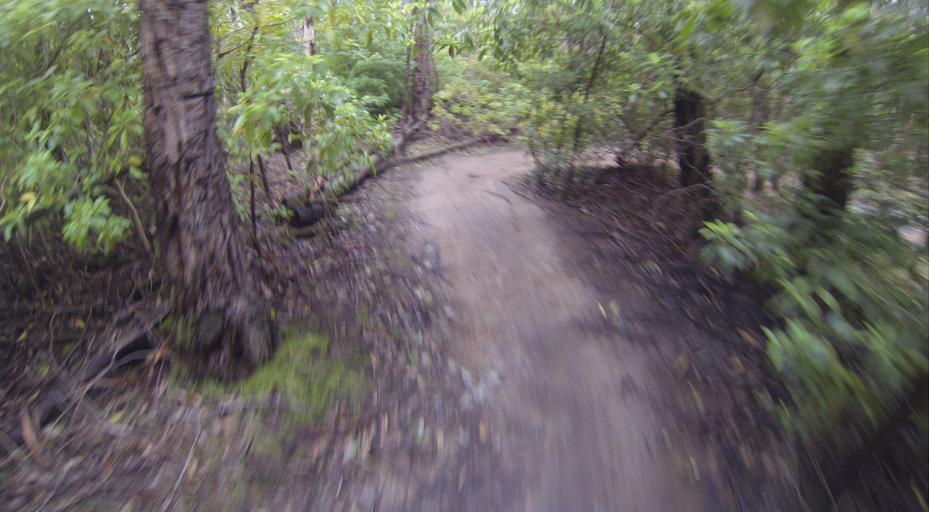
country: AU
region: Victoria
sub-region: Yarra Ranges
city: Lysterfield
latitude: -37.9401
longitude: 145.3034
